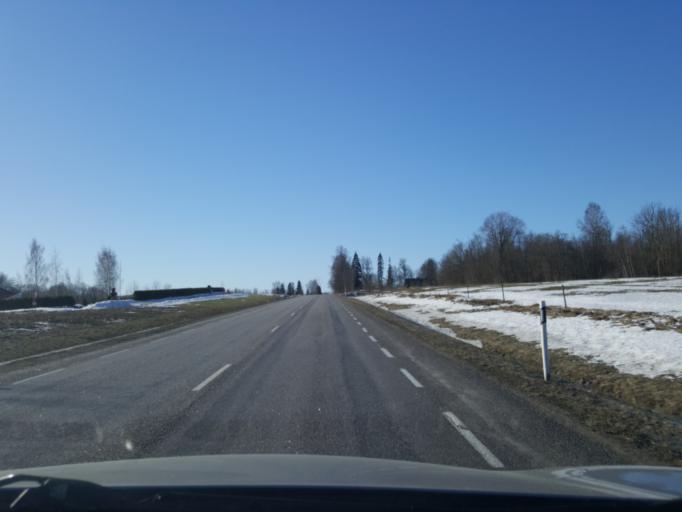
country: EE
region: Viljandimaa
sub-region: Viiratsi vald
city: Viiratsi
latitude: 58.4000
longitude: 25.6498
